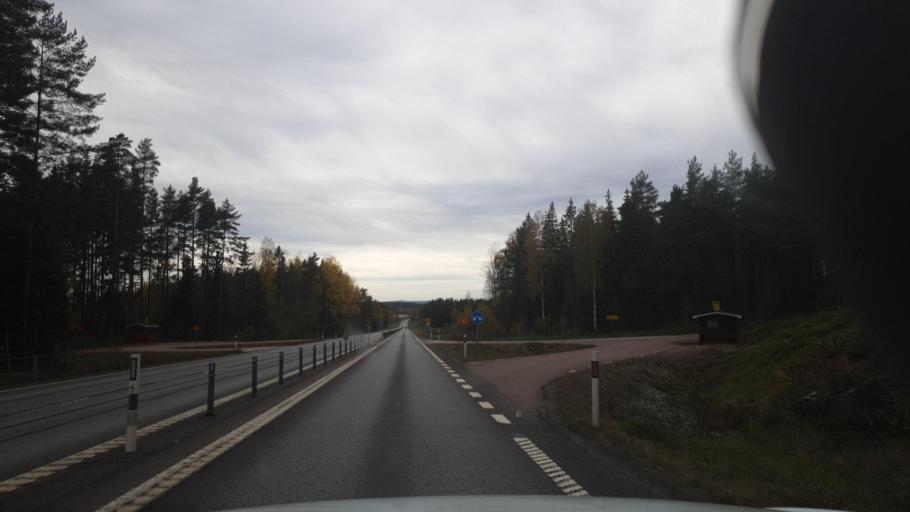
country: SE
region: Vaermland
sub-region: Arvika Kommun
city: Arvika
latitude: 59.6493
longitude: 12.6829
